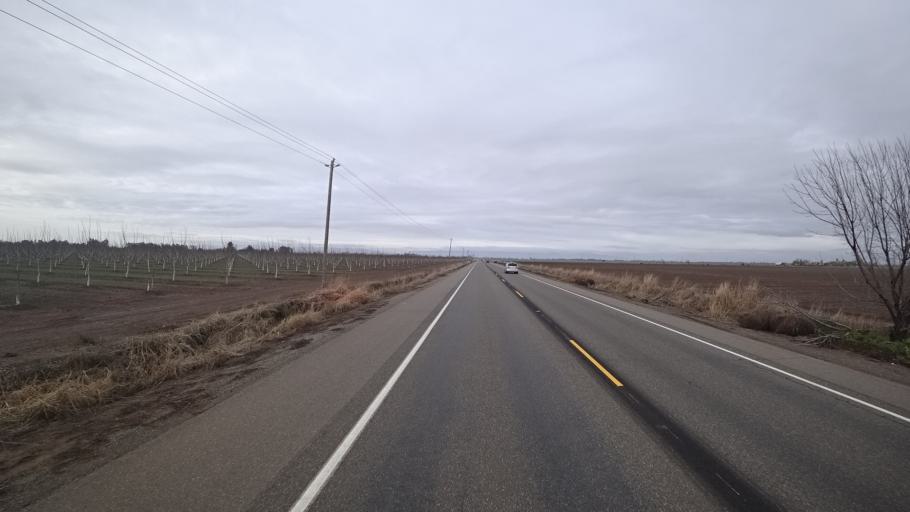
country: US
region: California
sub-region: Yolo County
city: Davis
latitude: 38.5614
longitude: -121.7961
